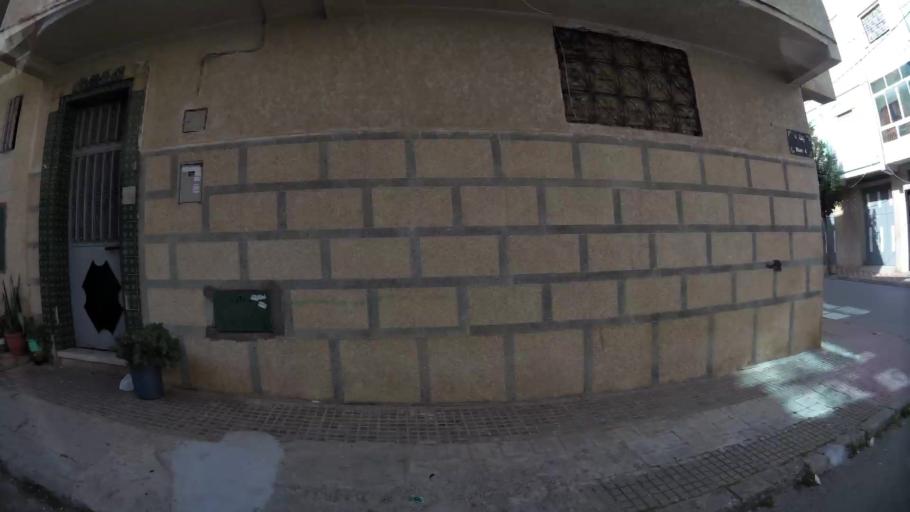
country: MA
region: Tanger-Tetouan
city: Tetouan
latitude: 35.5912
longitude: -5.3523
